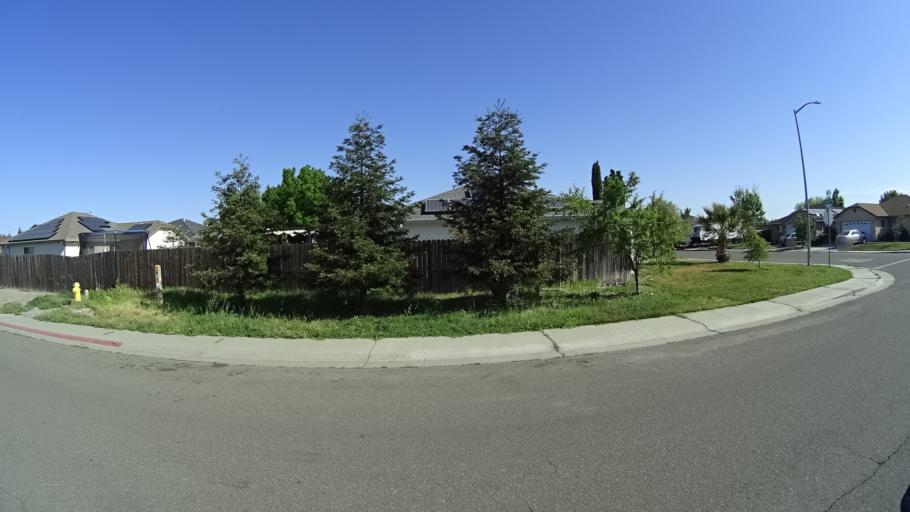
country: US
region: California
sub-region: Glenn County
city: Orland
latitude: 39.7509
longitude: -122.1751
